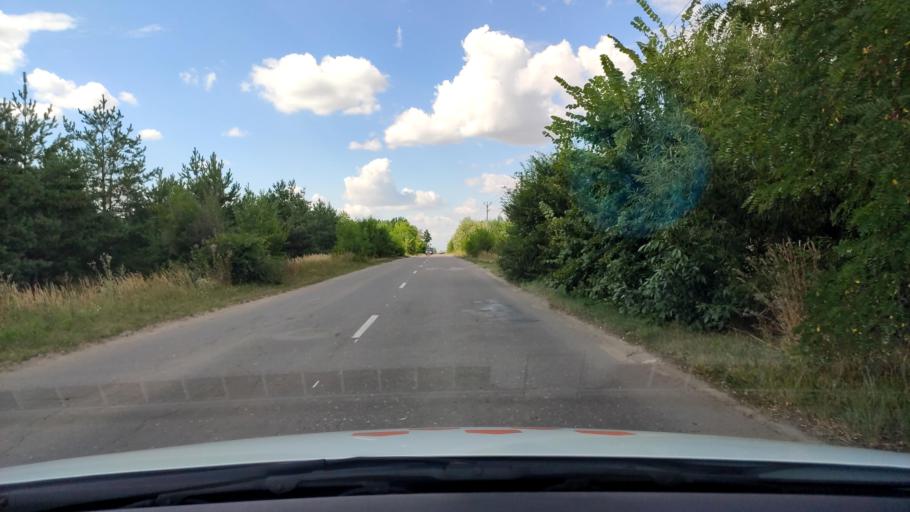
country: RU
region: Voronezj
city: Podgornoye
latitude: 51.8337
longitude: 39.2035
